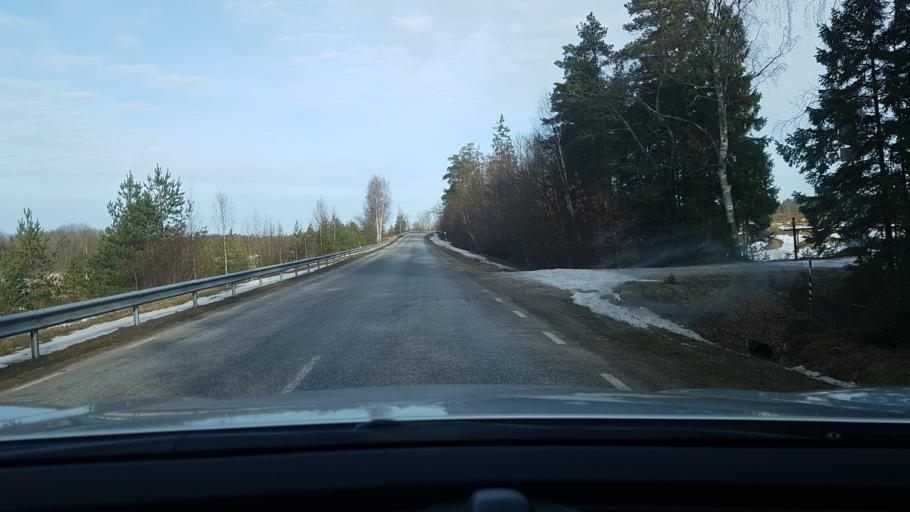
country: EE
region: Saare
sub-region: Kuressaare linn
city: Kuressaare
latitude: 58.4502
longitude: 22.7080
